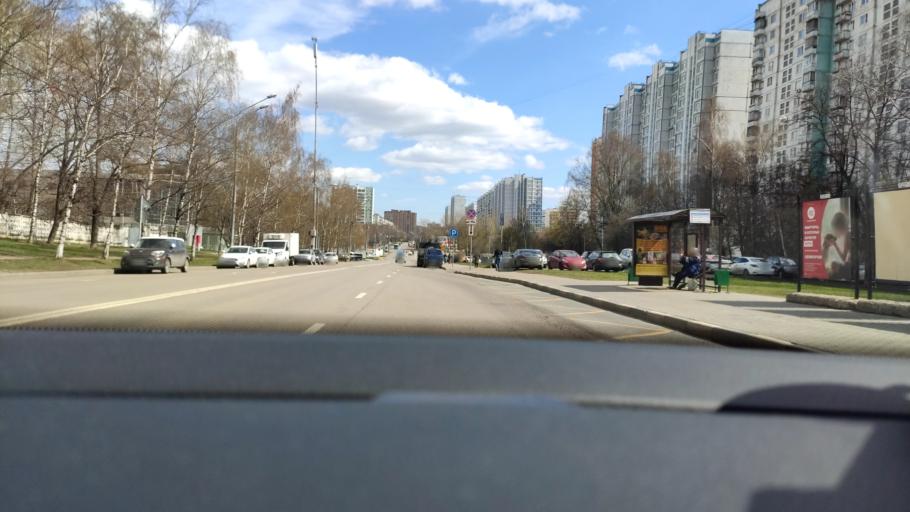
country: RU
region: Moscow
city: Zapadnoye Degunino
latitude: 55.8769
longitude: 37.5414
